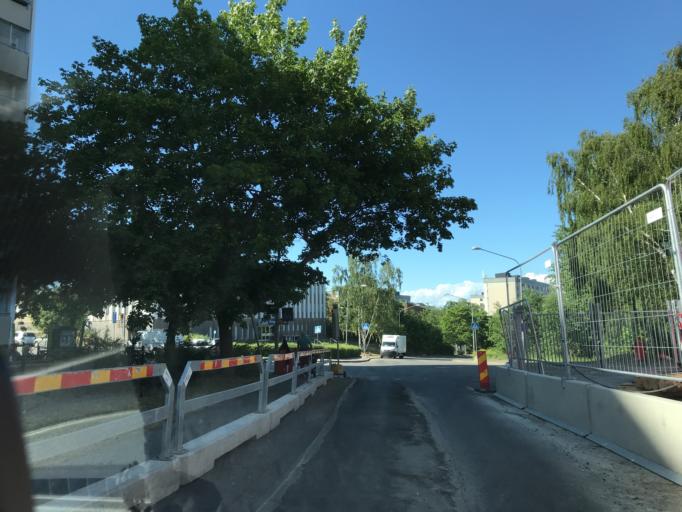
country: SE
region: Stockholm
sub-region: Huddinge Kommun
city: Segeltorp
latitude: 59.2945
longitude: 17.9414
